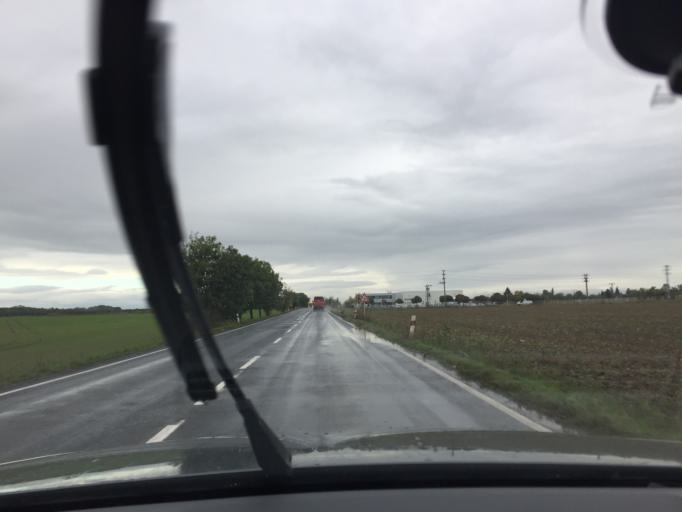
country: CZ
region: Central Bohemia
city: Klecany
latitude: 50.2049
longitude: 14.4316
